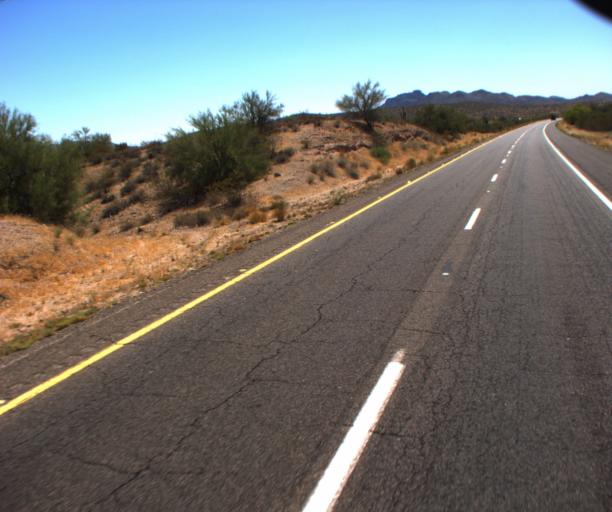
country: US
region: Arizona
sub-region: Maricopa County
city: Fountain Hills
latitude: 33.5852
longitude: -111.6094
